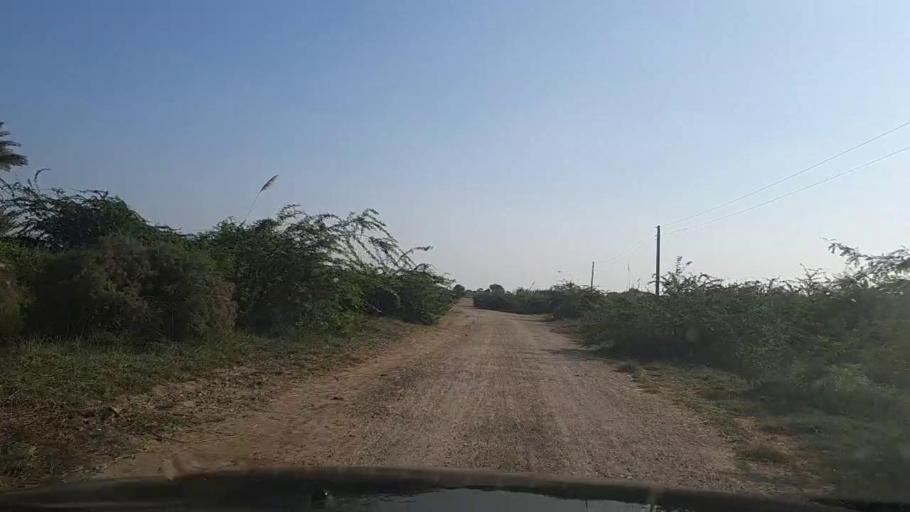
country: PK
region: Sindh
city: Gharo
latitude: 24.7089
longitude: 67.7040
